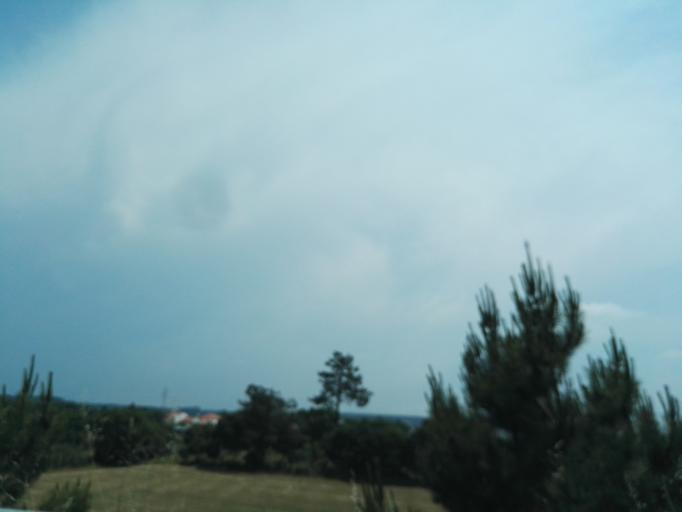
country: PT
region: Santarem
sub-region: Entroncamento
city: Entroncamento
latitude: 39.4665
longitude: -8.4567
